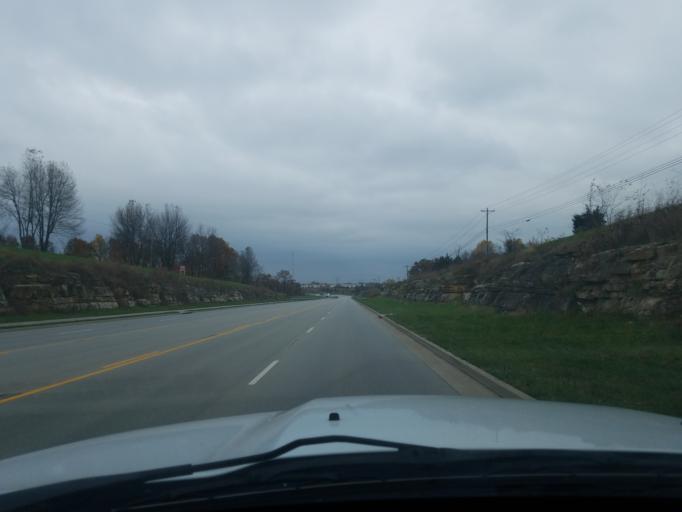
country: US
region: Kentucky
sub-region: Nelson County
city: Bardstown
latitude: 37.8076
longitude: -85.4298
